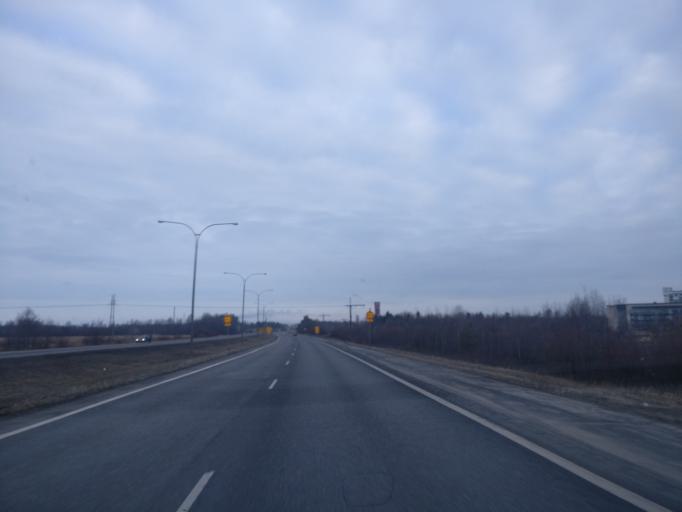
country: FI
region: Northern Ostrobothnia
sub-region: Oulu
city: Kempele
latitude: 64.9508
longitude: 25.5287
